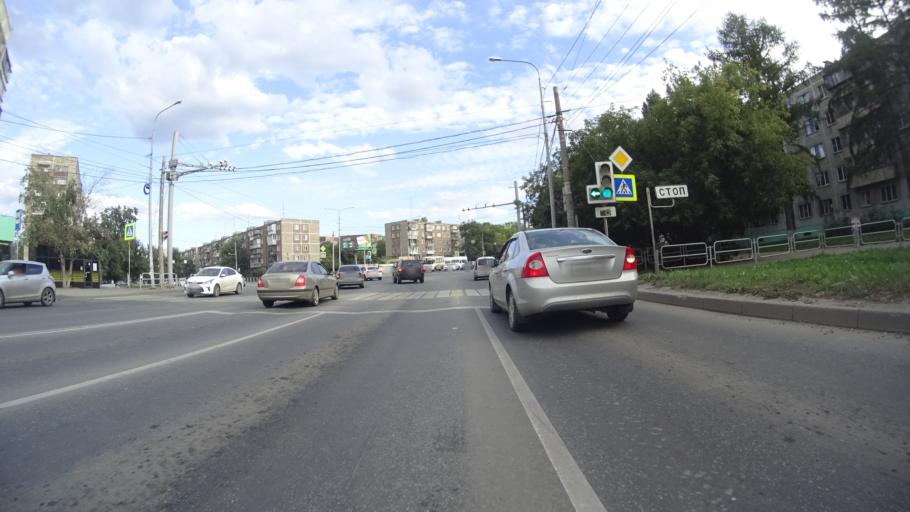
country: RU
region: Chelyabinsk
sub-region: Gorod Chelyabinsk
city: Chelyabinsk
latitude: 55.1988
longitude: 61.3313
